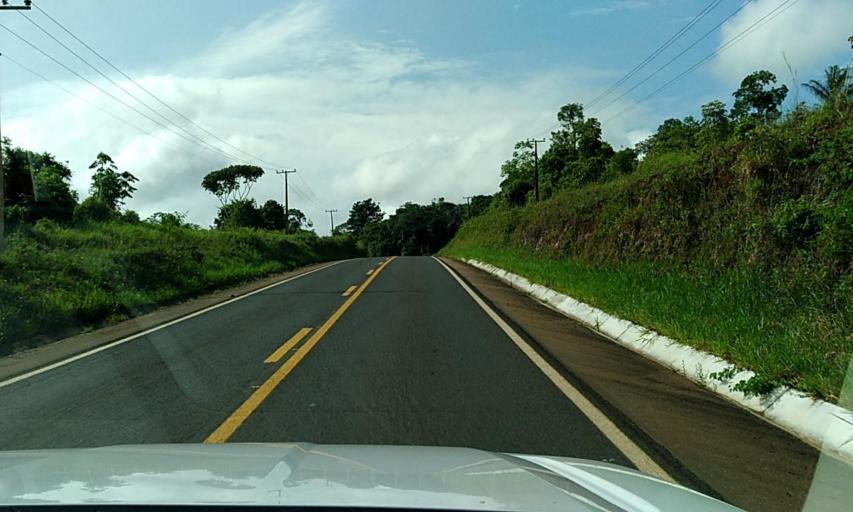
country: BR
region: Para
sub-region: Altamira
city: Altamira
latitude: -3.0934
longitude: -51.8783
